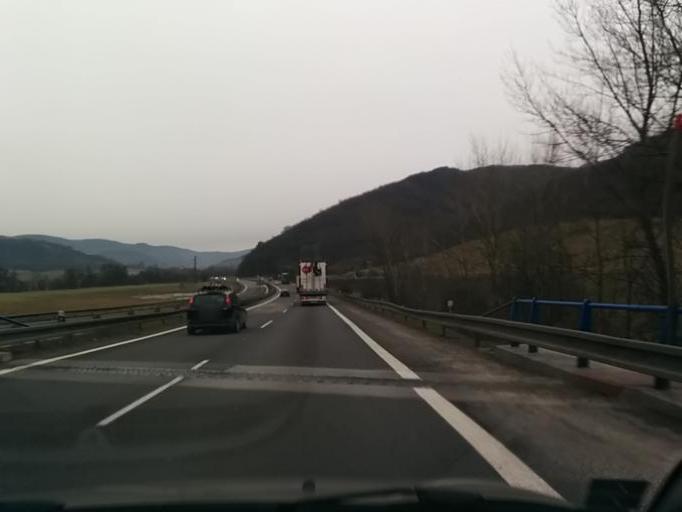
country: SK
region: Banskobystricky
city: Ziar nad Hronom
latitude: 48.5874
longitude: 18.9087
